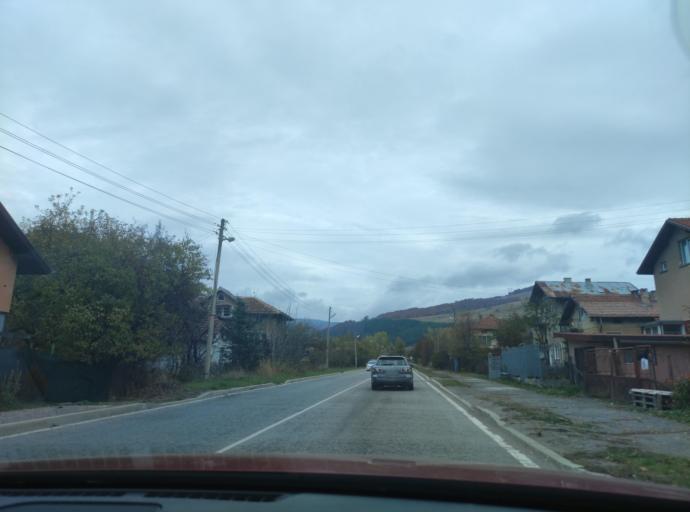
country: BG
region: Sofiya
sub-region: Obshtina Godech
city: Godech
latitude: 43.0748
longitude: 23.1080
